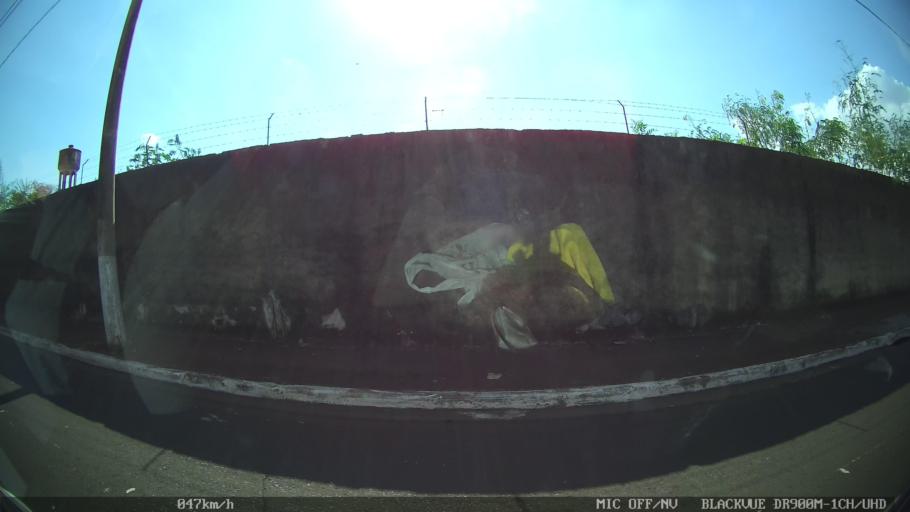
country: BR
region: Sao Paulo
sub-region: Ribeirao Preto
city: Ribeirao Preto
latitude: -21.1790
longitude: -47.8247
